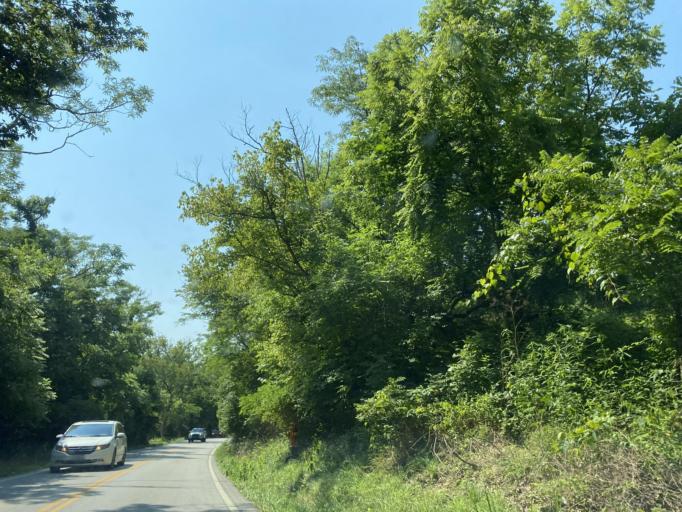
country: US
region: Kentucky
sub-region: Kenton County
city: Ryland Heights
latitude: 38.9110
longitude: -84.4506
